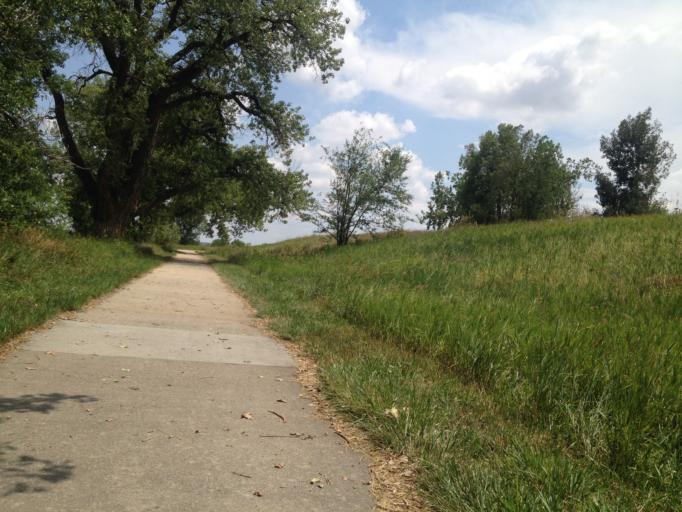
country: US
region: Colorado
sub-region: Boulder County
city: Louisville
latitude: 39.9719
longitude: -105.1480
